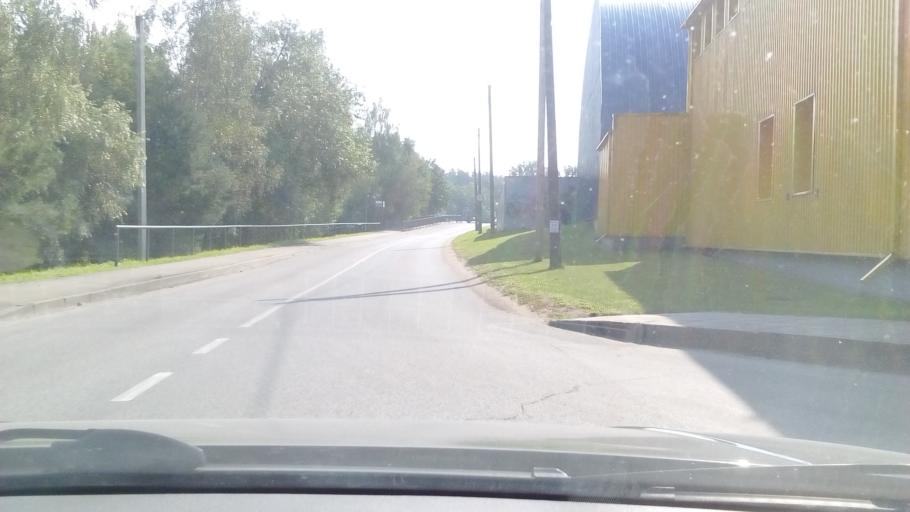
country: LT
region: Alytaus apskritis
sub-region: Alytus
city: Alytus
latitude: 54.3900
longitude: 24.0611
